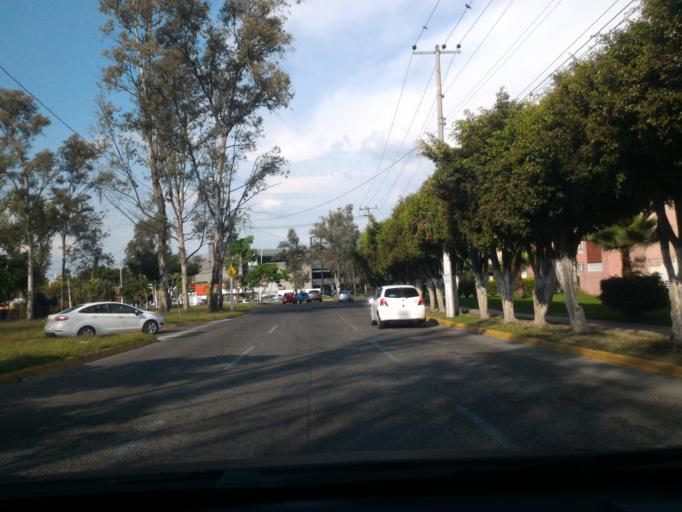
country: MX
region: Jalisco
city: Guadalajara
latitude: 20.6603
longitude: -103.4313
